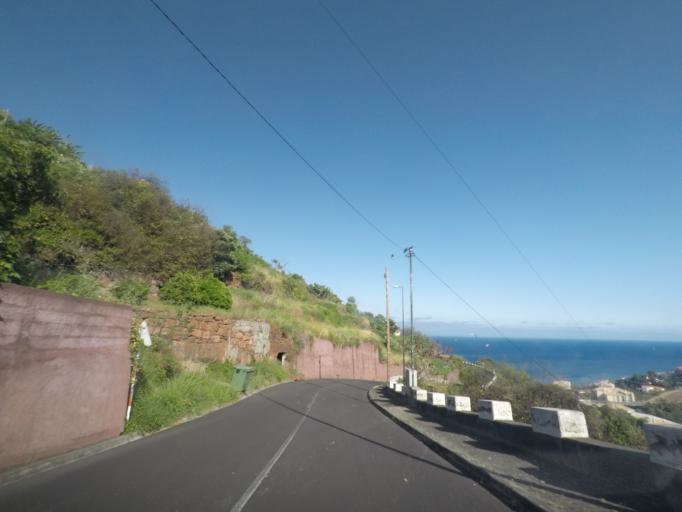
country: PT
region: Madeira
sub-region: Santa Cruz
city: Santa Cruz
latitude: 32.6925
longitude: -16.7967
